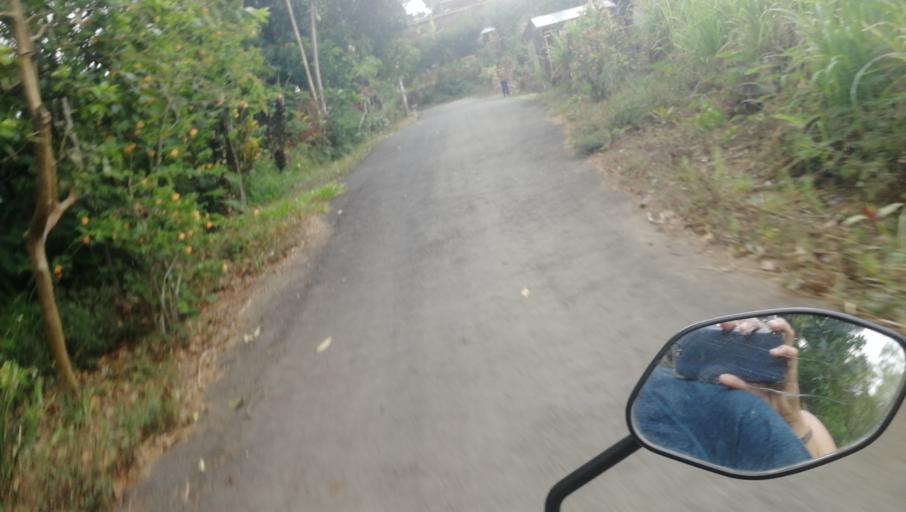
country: ID
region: Bali
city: Banjar Ambengan
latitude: -8.2087
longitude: 115.1104
